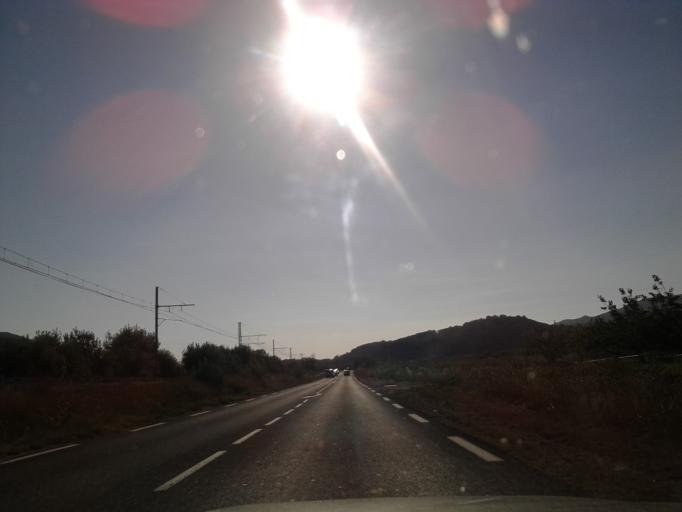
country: FR
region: Languedoc-Roussillon
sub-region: Departement des Pyrenees-Orientales
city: Vinca
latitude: 42.6440
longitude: 2.4935
